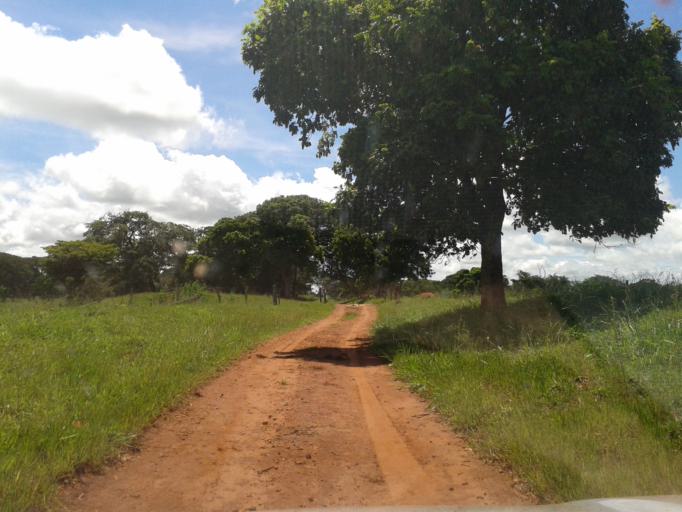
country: BR
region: Minas Gerais
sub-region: Santa Vitoria
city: Santa Vitoria
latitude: -18.7925
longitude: -49.8573
